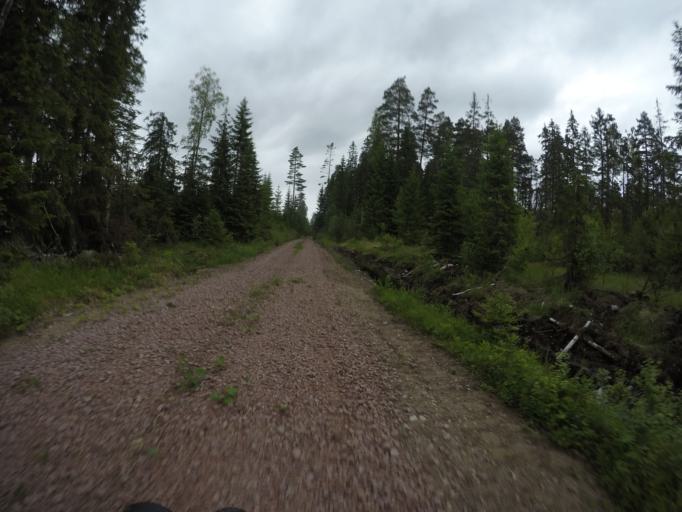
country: SE
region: OErebro
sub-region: Hallefors Kommun
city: Haellefors
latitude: 60.0233
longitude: 14.5751
